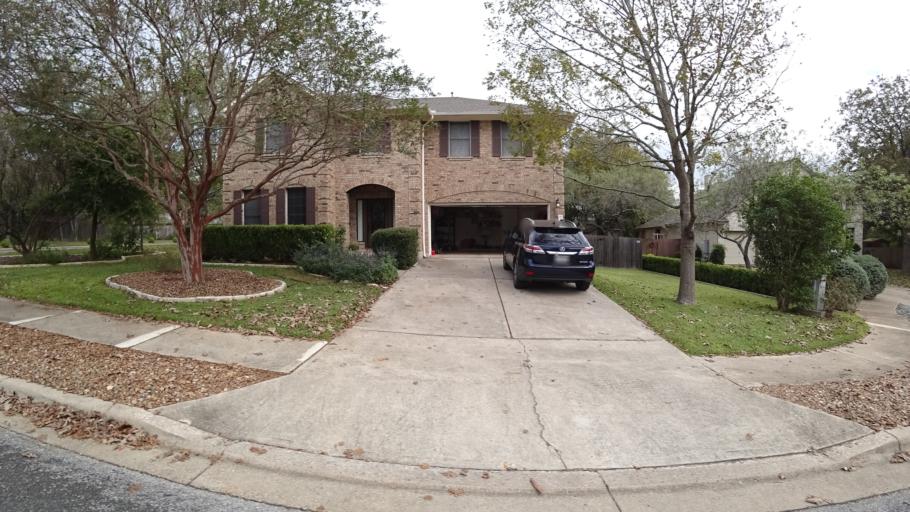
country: US
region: Texas
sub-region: Travis County
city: Shady Hollow
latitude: 30.1561
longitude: -97.8495
